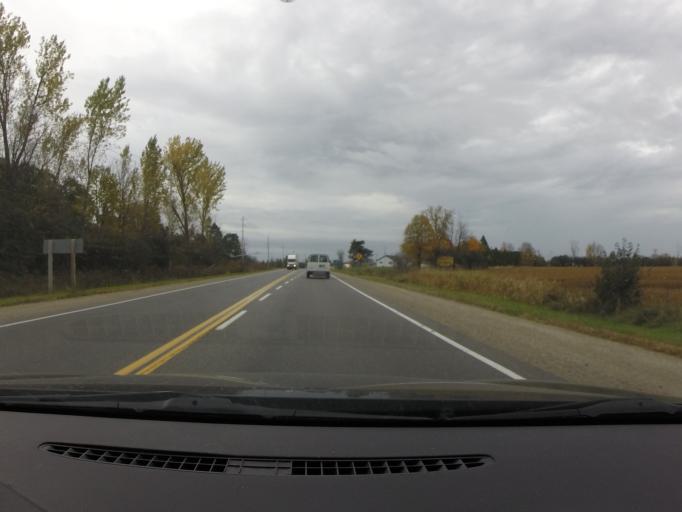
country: CA
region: Ontario
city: Perth
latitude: 44.9396
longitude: -76.2396
